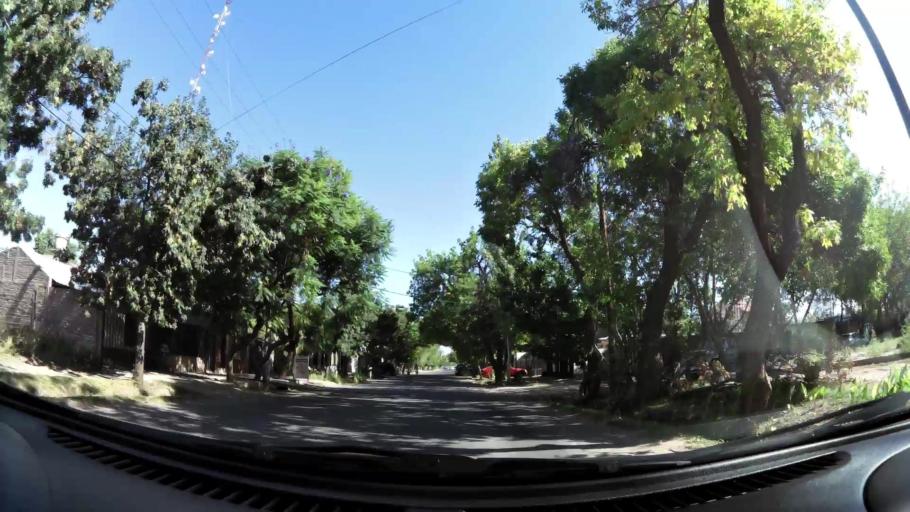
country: AR
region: Mendoza
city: Villa Nueva
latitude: -32.9217
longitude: -68.8013
